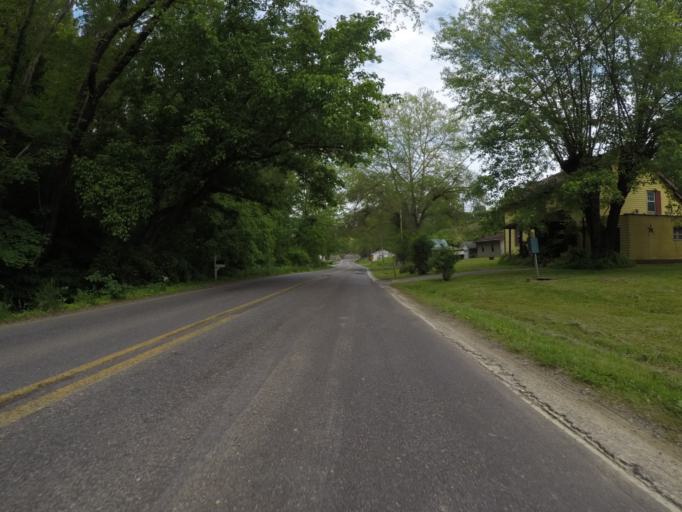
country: US
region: West Virginia
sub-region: Wayne County
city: Ceredo
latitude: 38.3554
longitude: -82.5575
